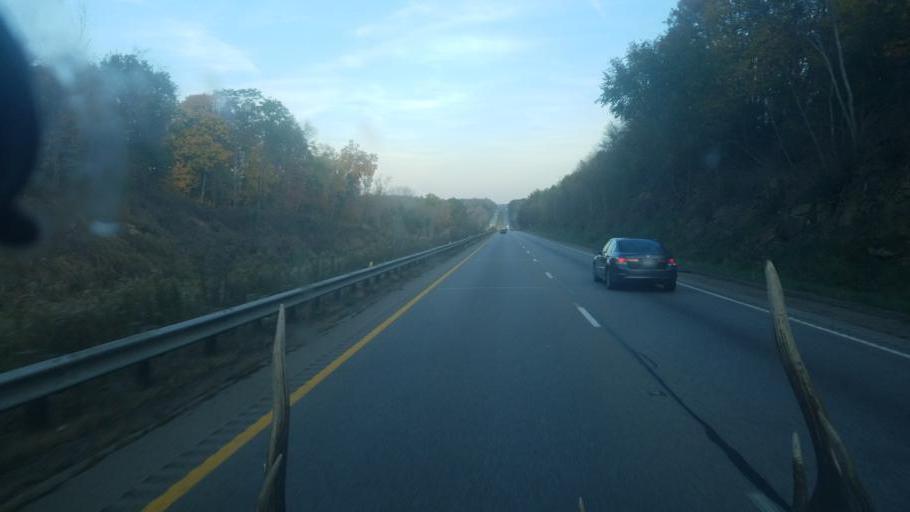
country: US
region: Ohio
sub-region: Perry County
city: Thornport
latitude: 39.9378
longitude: -82.2968
